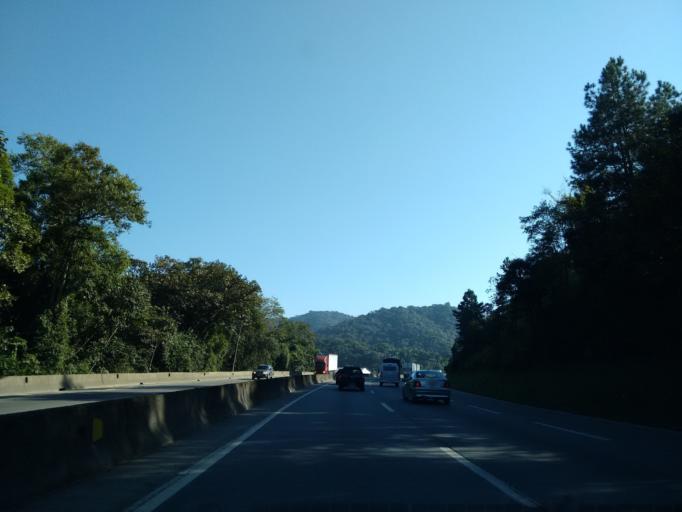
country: BR
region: Santa Catarina
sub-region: Joinville
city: Joinville
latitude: -26.2345
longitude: -48.9160
